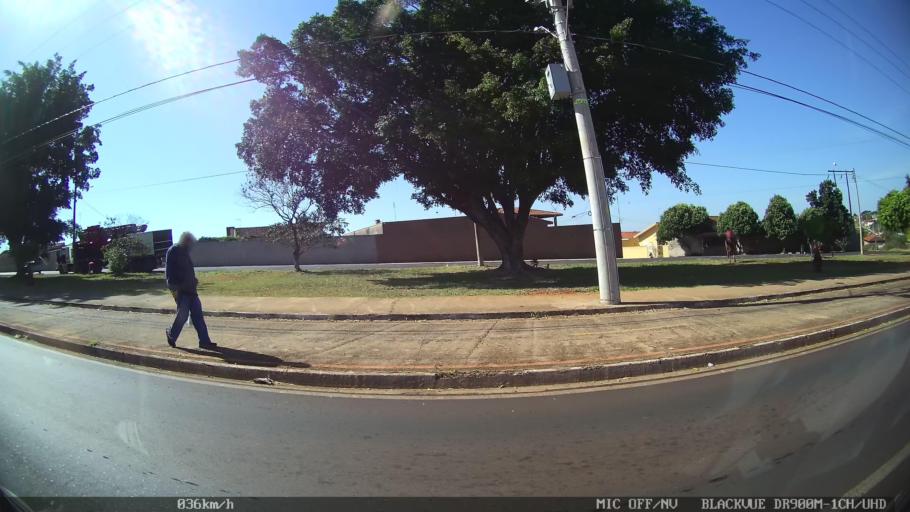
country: BR
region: Sao Paulo
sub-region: Batatais
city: Batatais
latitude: -20.9057
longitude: -47.5821
